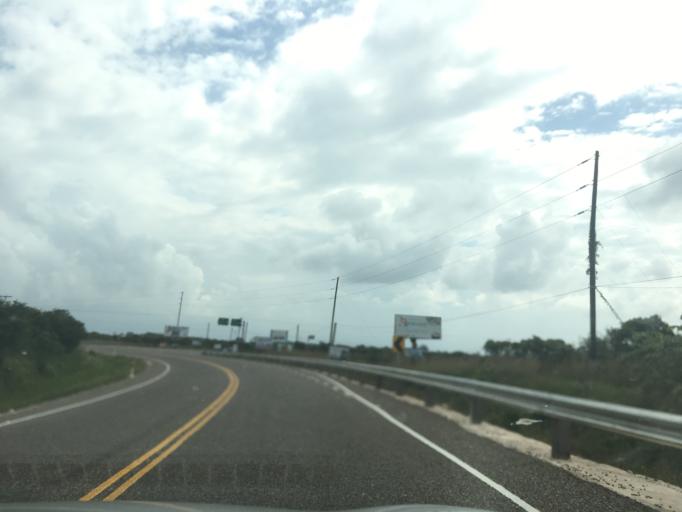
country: BZ
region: Stann Creek
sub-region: Dangriga
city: Dangriga
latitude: 16.9818
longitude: -88.2958
